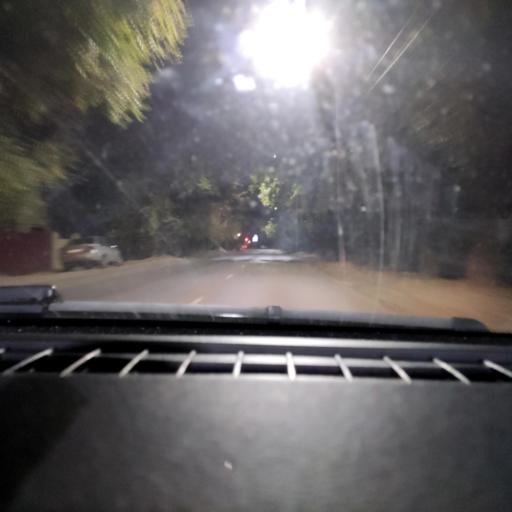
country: RU
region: Voronezj
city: Maslovka
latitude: 51.6328
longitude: 39.2626
